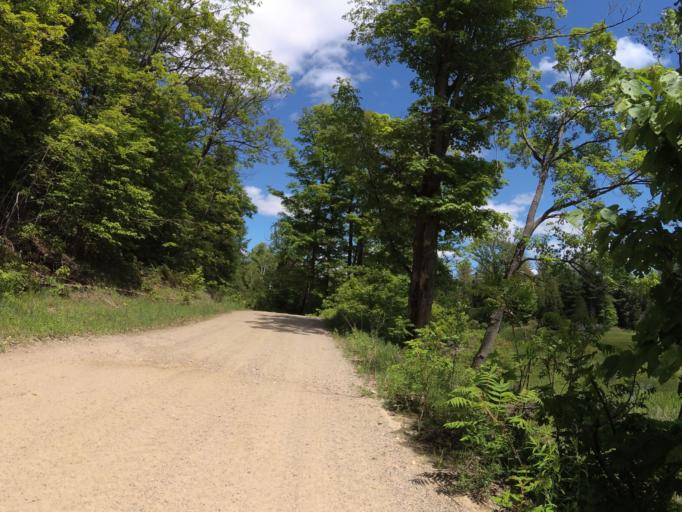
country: CA
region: Ontario
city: Renfrew
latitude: 45.0045
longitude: -76.9033
